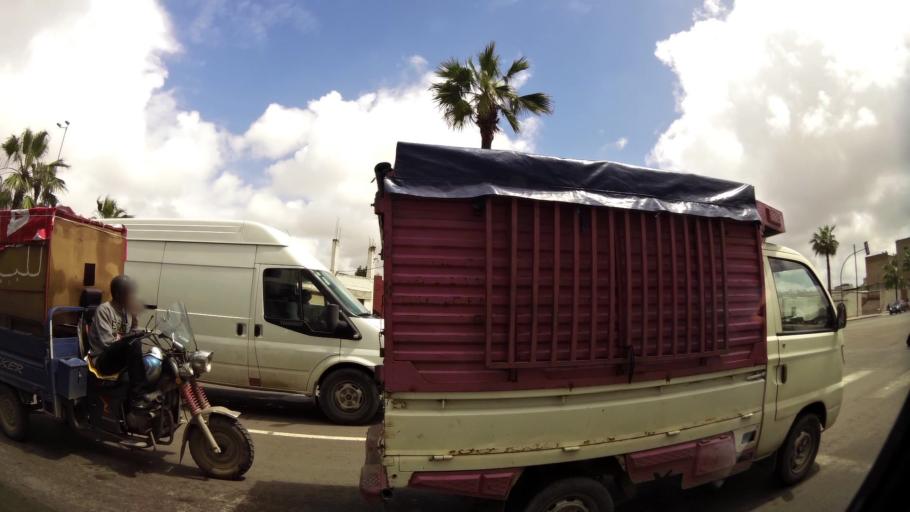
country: MA
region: Grand Casablanca
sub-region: Casablanca
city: Casablanca
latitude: 33.5675
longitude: -7.5959
